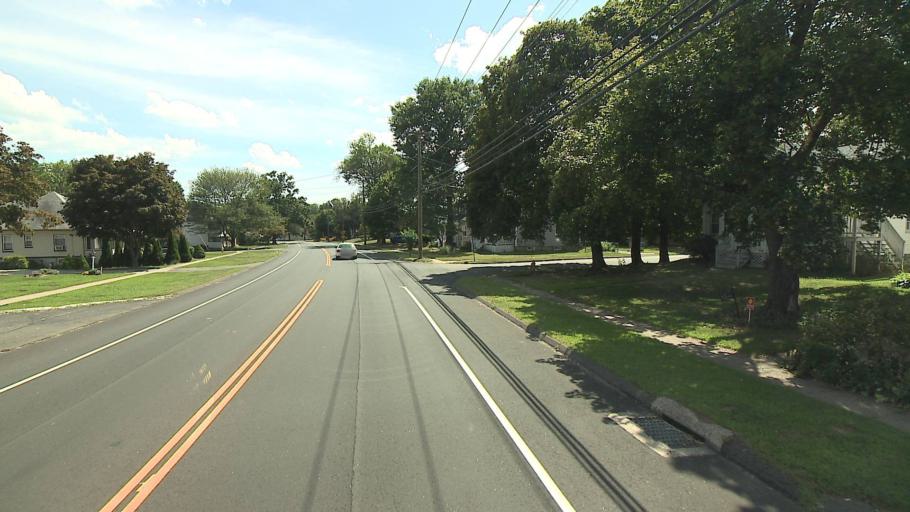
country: US
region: Connecticut
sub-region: Fairfield County
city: Stratford
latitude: 41.2136
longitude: -73.1458
